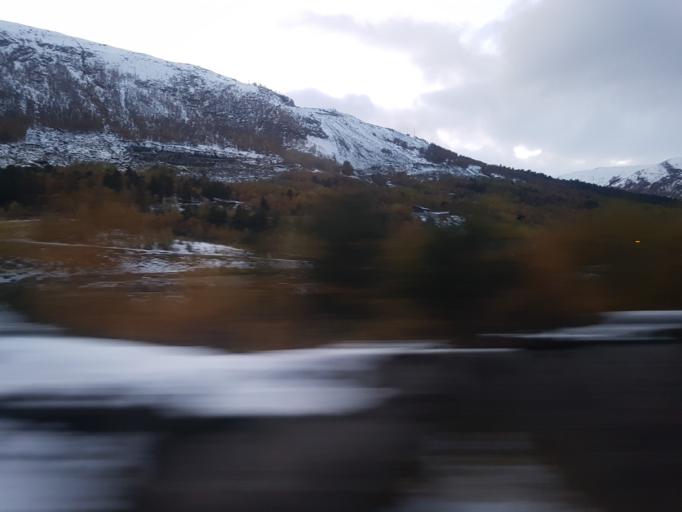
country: NO
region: Sor-Trondelag
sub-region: Oppdal
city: Oppdal
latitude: 62.4272
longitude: 9.6122
